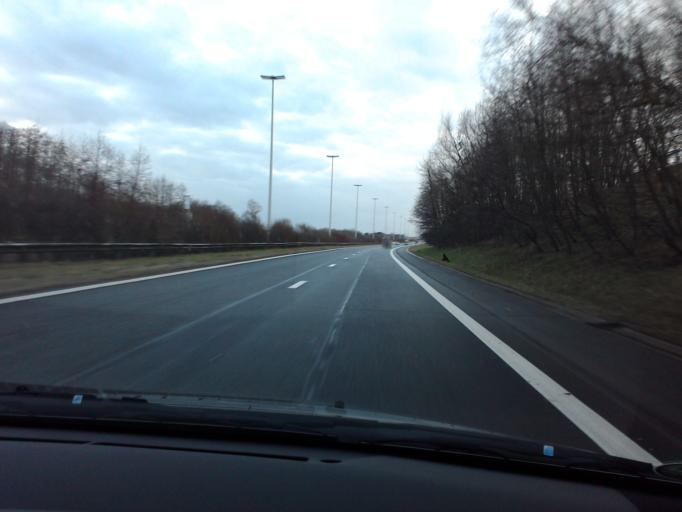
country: BE
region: Wallonia
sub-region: Province de Liege
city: Chaudfontaine
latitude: 50.5501
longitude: 5.6520
